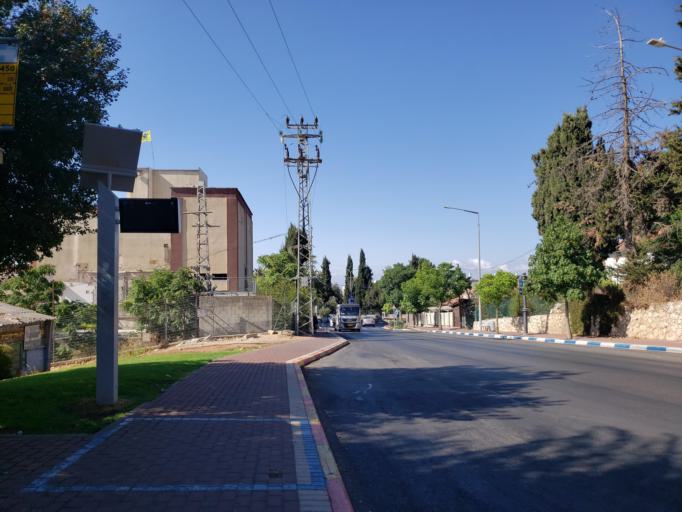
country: IL
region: Northern District
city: Safed
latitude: 32.9605
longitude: 35.4982
